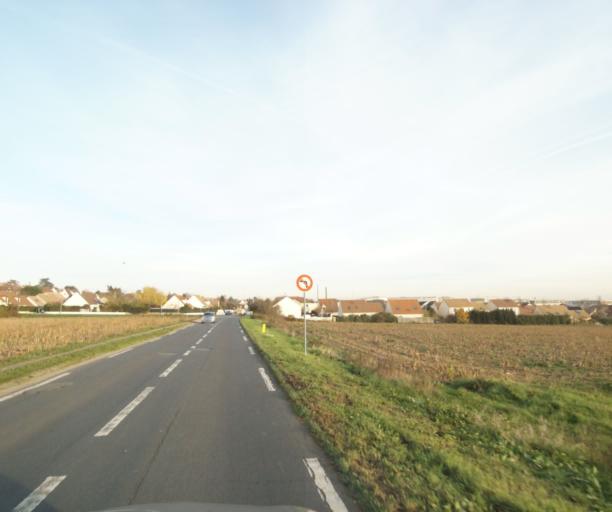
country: FR
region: Ile-de-France
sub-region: Departement des Yvelines
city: Chanteloup-les-Vignes
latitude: 48.9753
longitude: 2.0224
